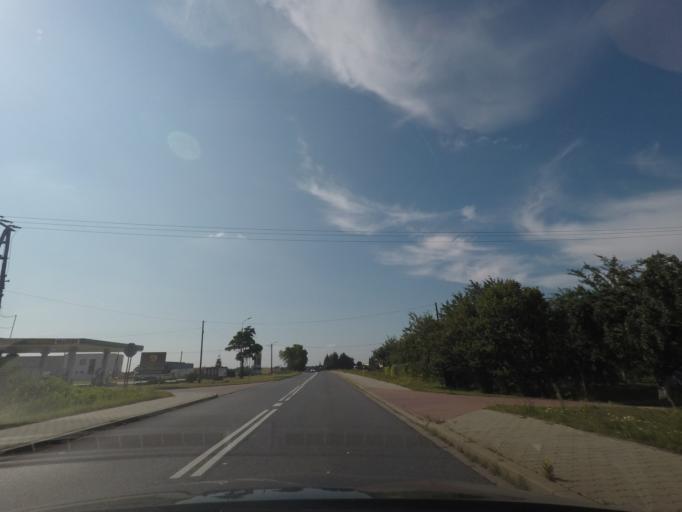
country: PL
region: Silesian Voivodeship
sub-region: Powiat pszczynski
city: Radostowice
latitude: 50.0071
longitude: 18.8688
